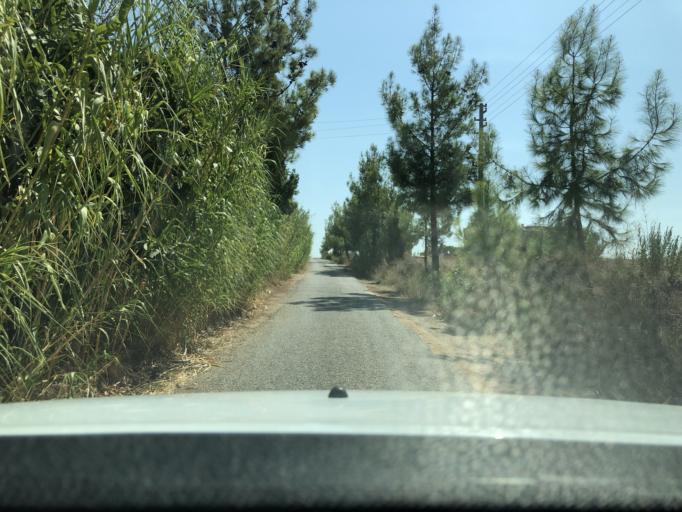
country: TR
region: Antalya
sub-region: Manavgat
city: Manavgat
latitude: 36.8042
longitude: 31.4743
